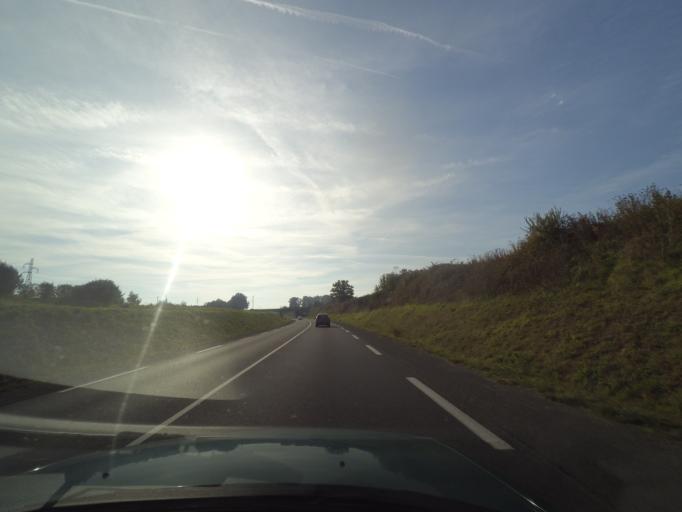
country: FR
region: Pays de la Loire
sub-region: Departement de la Vendee
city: Bouffere
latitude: 46.9654
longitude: -1.3275
